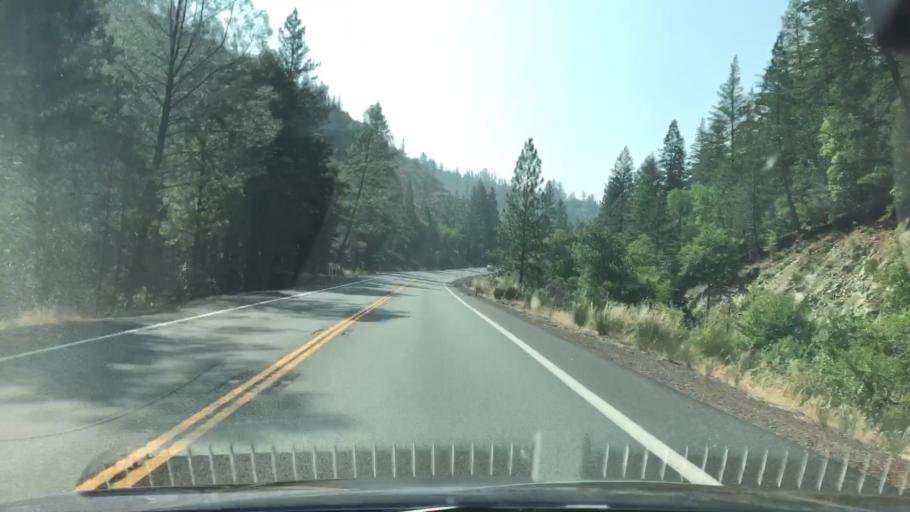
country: US
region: California
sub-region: Lake County
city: Middletown
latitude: 38.6849
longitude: -122.5939
